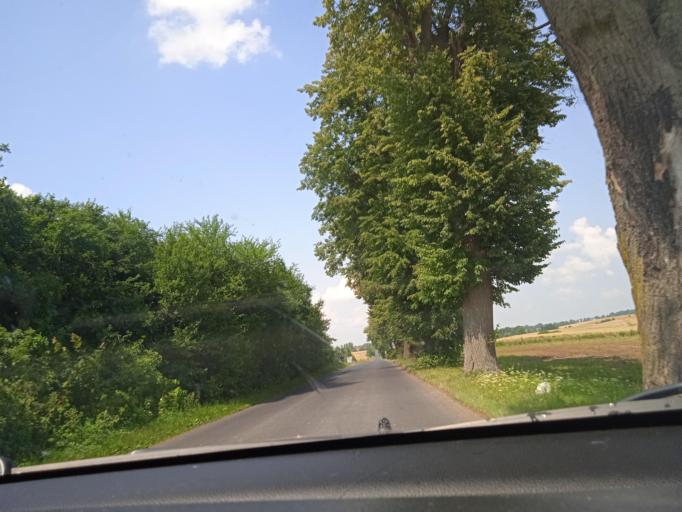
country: PL
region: Kujawsko-Pomorskie
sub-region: Powiat grudziadzki
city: Lasin
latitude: 53.5374
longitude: 19.0691
